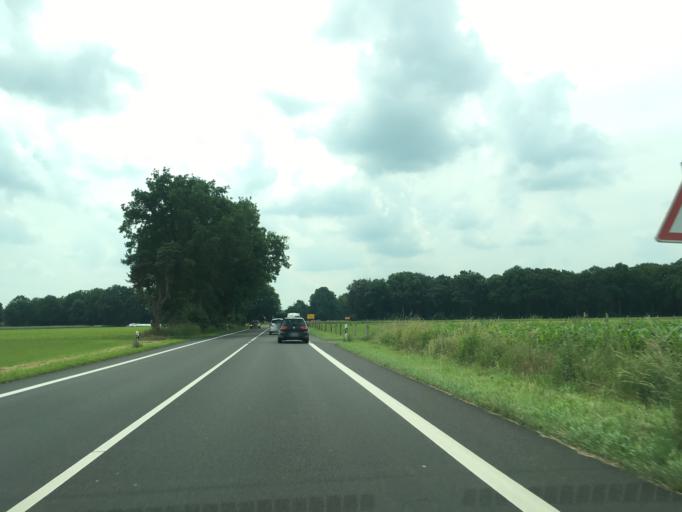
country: DE
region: North Rhine-Westphalia
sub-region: Regierungsbezirk Munster
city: Steinfurt
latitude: 52.1720
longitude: 7.3497
